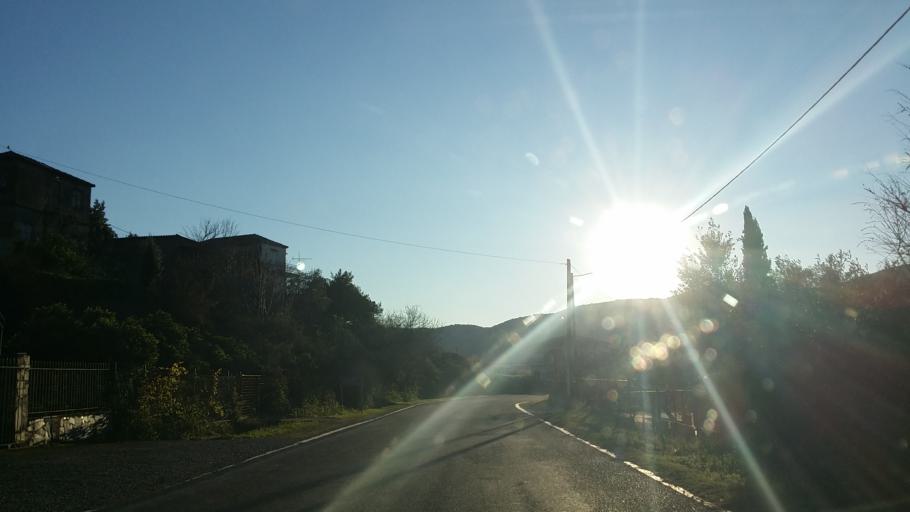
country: GR
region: West Greece
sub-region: Nomos Aitolias kai Akarnanias
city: Lepenou
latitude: 38.7388
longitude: 21.3459
